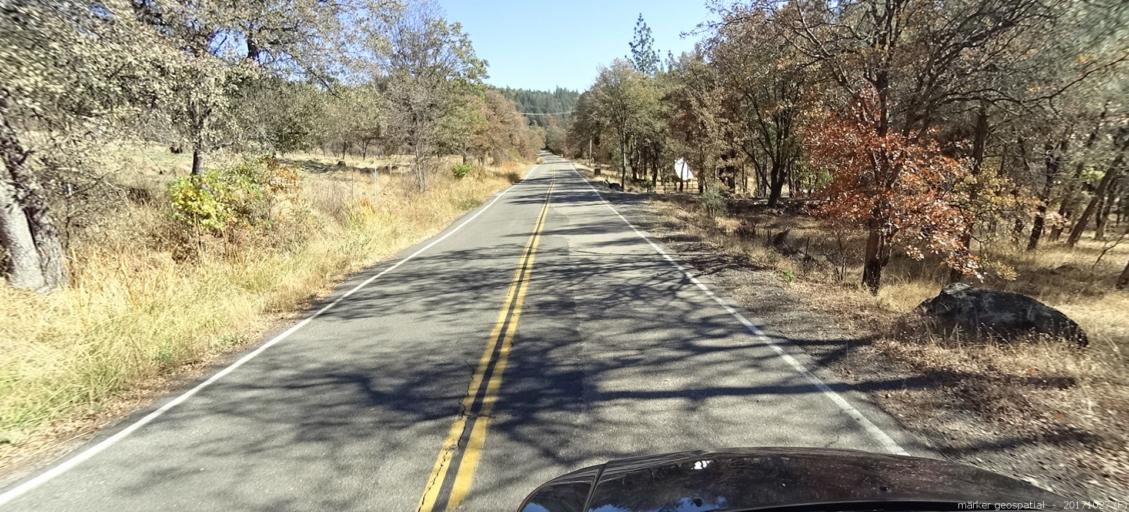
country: US
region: California
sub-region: Shasta County
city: Shingletown
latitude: 40.7044
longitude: -121.9243
